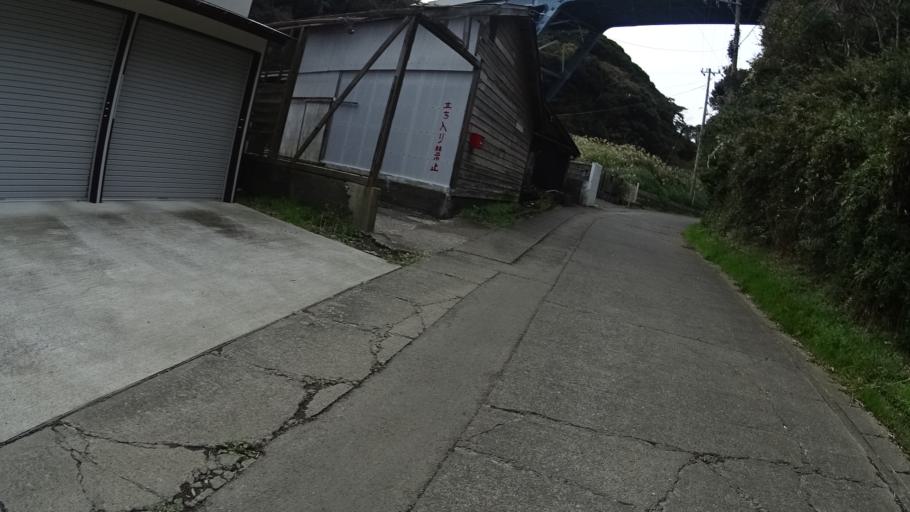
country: JP
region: Kanagawa
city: Miura
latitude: 35.1422
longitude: 139.6367
